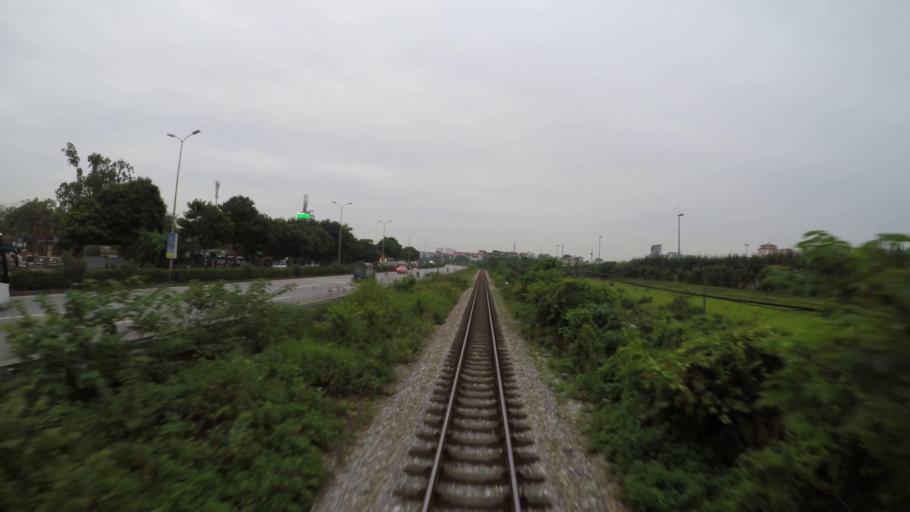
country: VN
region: Ha Noi
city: Trau Quy
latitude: 21.0100
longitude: 105.9535
